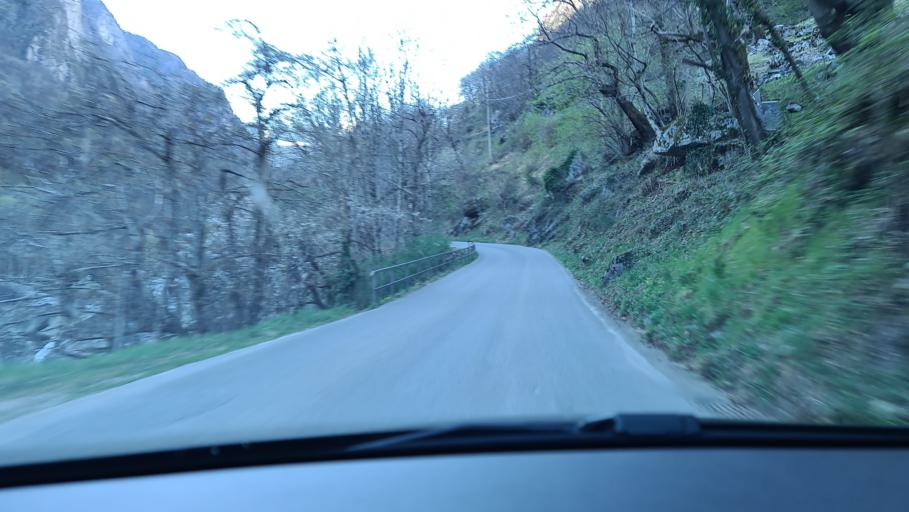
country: CH
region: Ticino
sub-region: Vallemaggia District
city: Cevio
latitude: 46.3482
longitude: 8.5990
